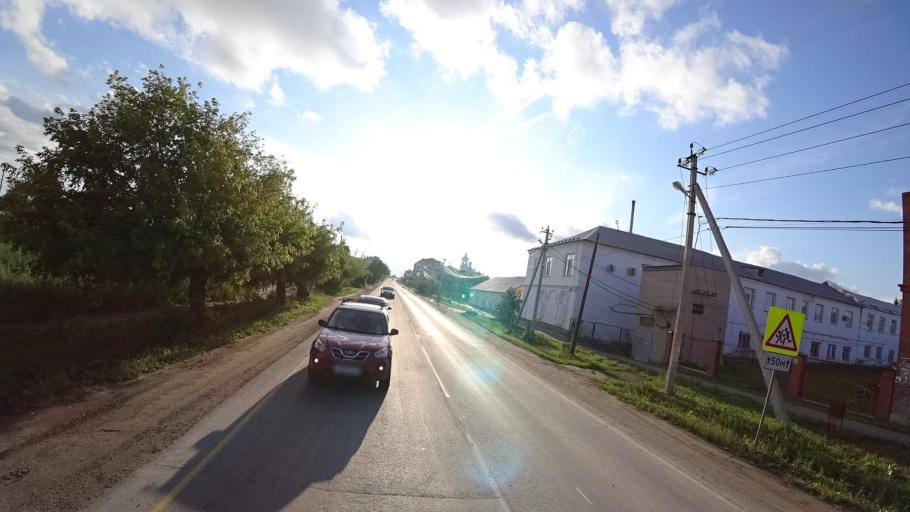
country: RU
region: Sverdlovsk
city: Kamyshlov
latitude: 56.8447
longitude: 62.6975
